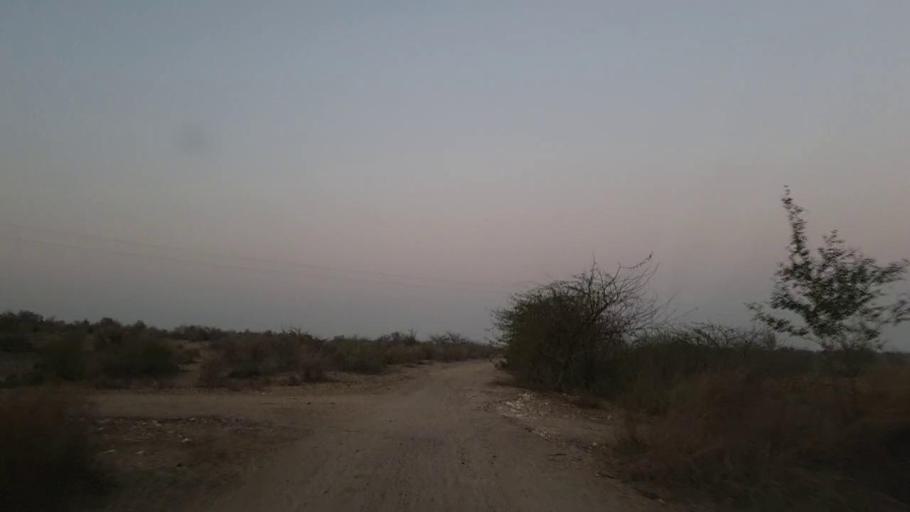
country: PK
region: Sindh
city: Bandhi
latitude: 26.6090
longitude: 68.3886
